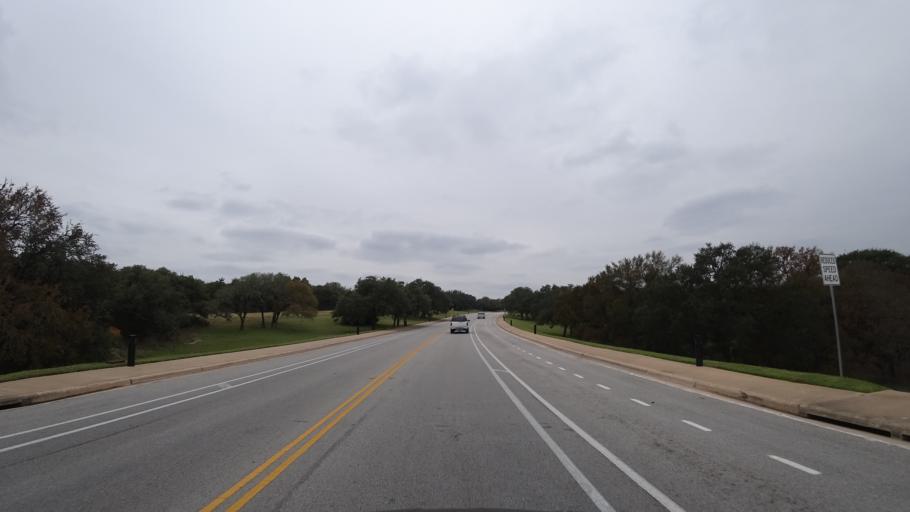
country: US
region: Texas
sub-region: Travis County
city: Shady Hollow
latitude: 30.1963
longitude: -97.8804
